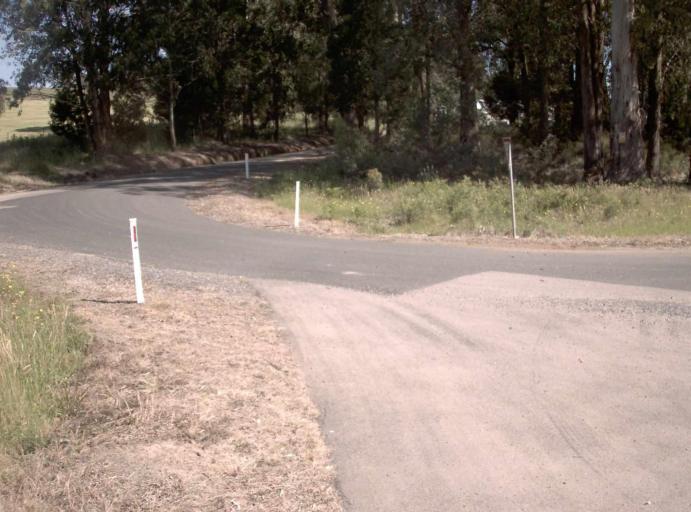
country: AU
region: New South Wales
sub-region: Bombala
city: Bombala
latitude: -37.1894
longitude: 148.7270
